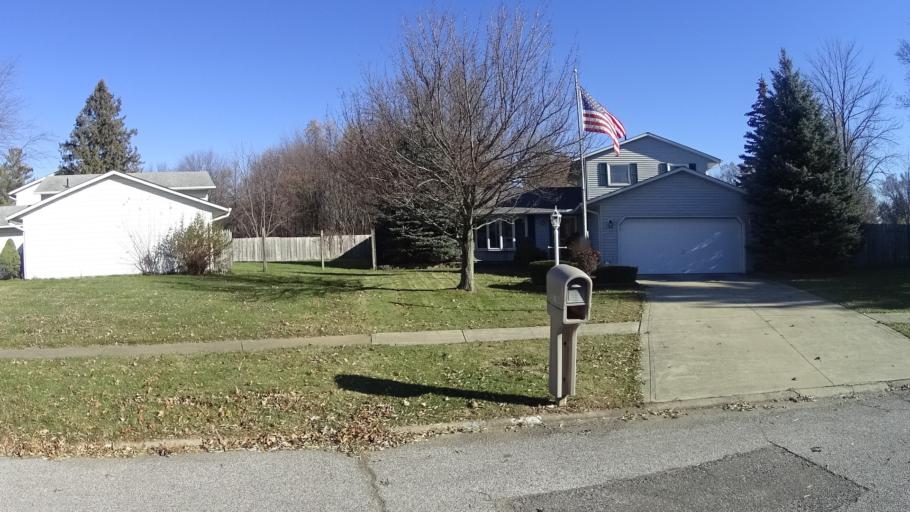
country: US
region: Ohio
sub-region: Lorain County
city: Elyria
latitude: 41.3614
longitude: -82.1616
